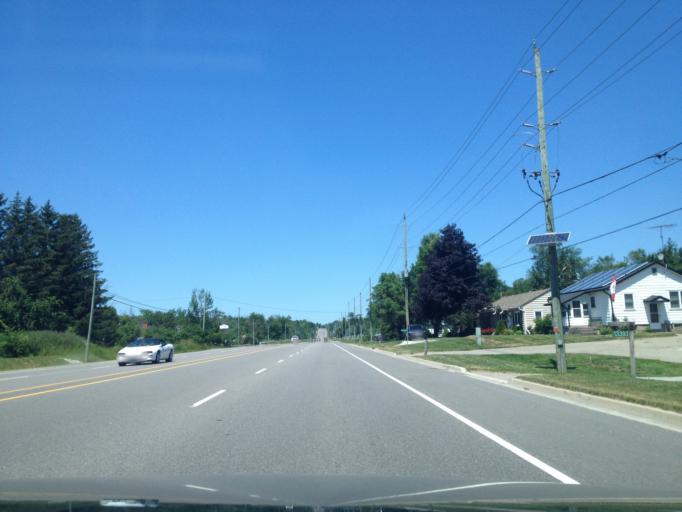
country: CA
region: Ontario
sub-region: Halton
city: Milton
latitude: 43.6592
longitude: -79.9627
